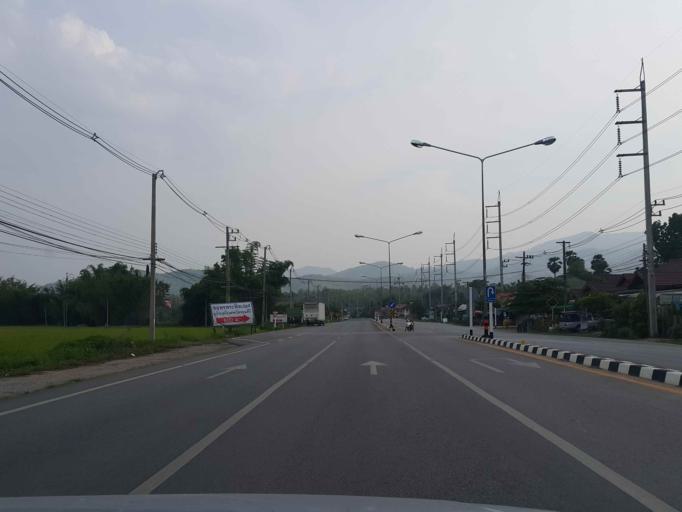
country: TH
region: Chiang Mai
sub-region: Amphoe Chiang Dao
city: Chiang Dao
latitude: 19.3304
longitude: 98.9553
